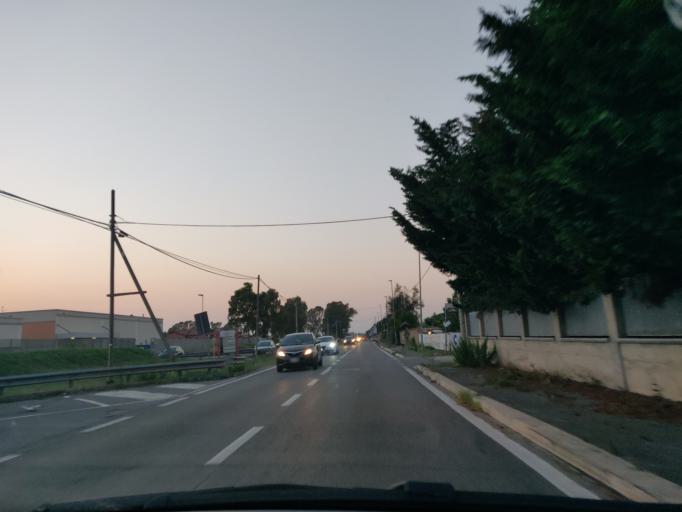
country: IT
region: Latium
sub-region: Citta metropolitana di Roma Capitale
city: Npp 23 (Parco Leonardo)
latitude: 41.8112
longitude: 12.3037
